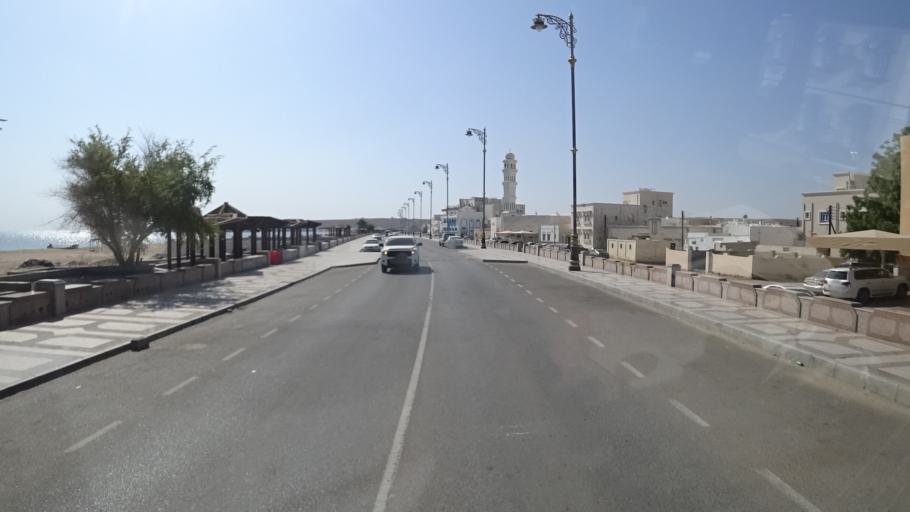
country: OM
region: Ash Sharqiyah
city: Sur
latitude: 22.5715
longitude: 59.5291
